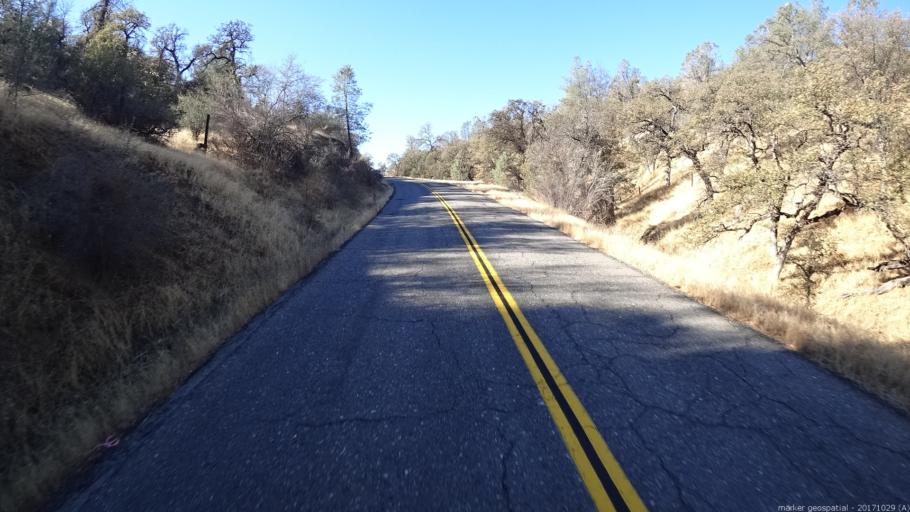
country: US
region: California
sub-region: Trinity County
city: Lewiston
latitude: 40.3939
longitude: -122.7950
